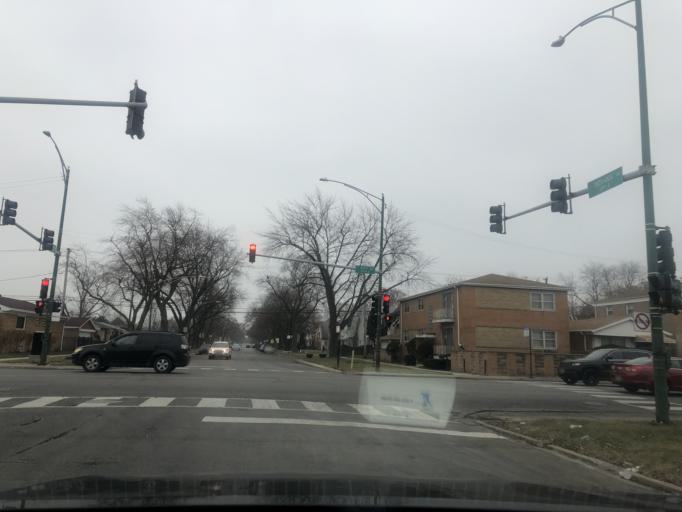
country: US
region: Illinois
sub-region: Cook County
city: Evergreen Park
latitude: 41.7367
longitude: -87.6193
